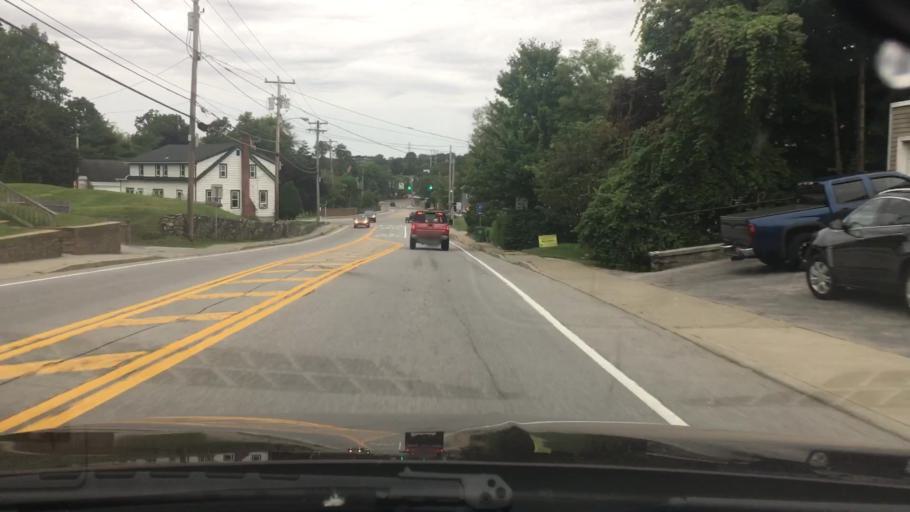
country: US
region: New York
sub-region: Dutchess County
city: Pleasant Valley
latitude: 41.7459
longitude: -73.8192
